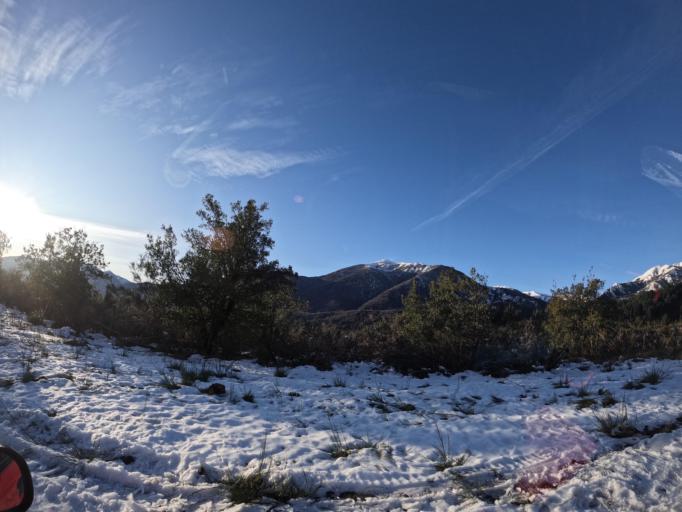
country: CL
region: Biobio
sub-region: Provincia de Nuble
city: Coihueco
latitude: -37.3674
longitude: -71.5024
